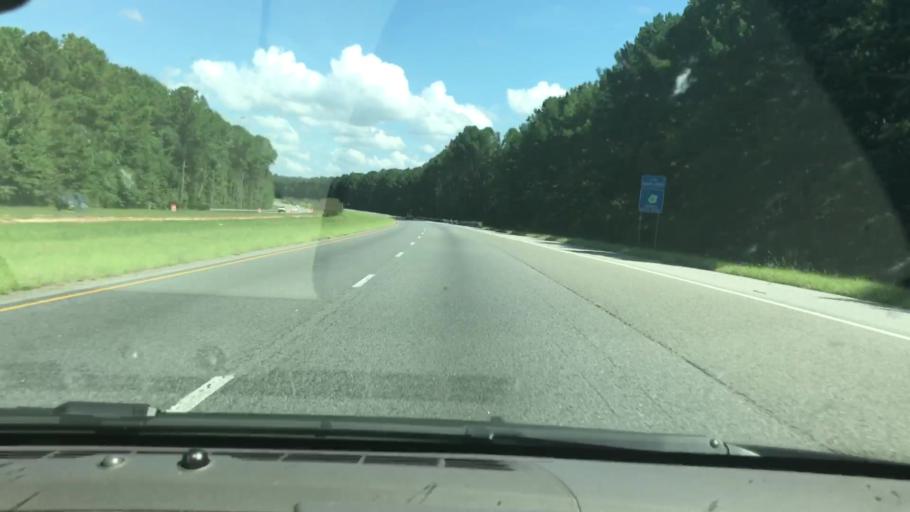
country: US
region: Georgia
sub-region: Harris County
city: Hamilton
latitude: 32.7522
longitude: -85.0164
